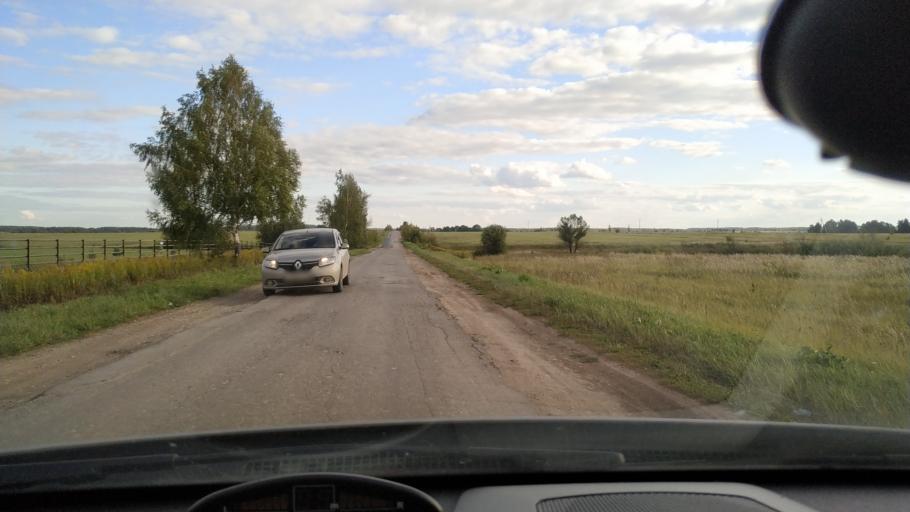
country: RU
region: Rjazan
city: Polyany
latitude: 54.5744
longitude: 39.8613
